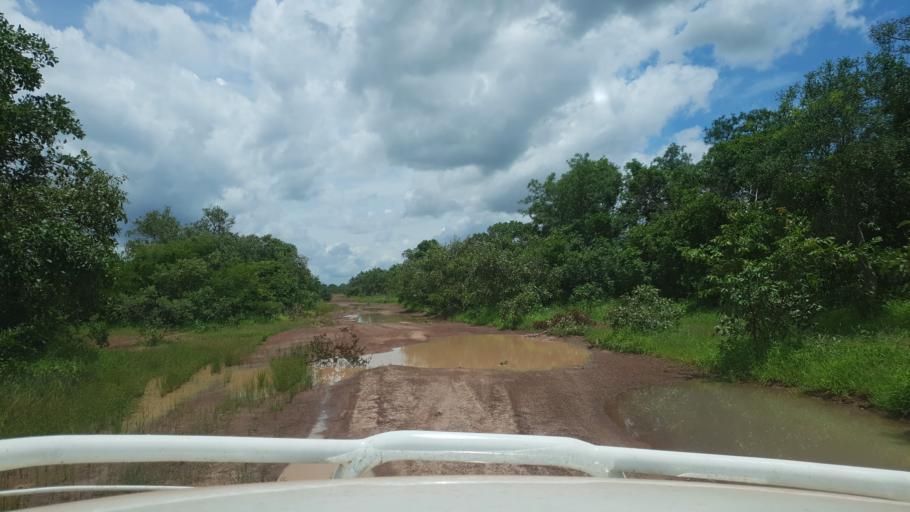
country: ML
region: Koulikoro
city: Banamba
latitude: 13.1992
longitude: -7.3300
